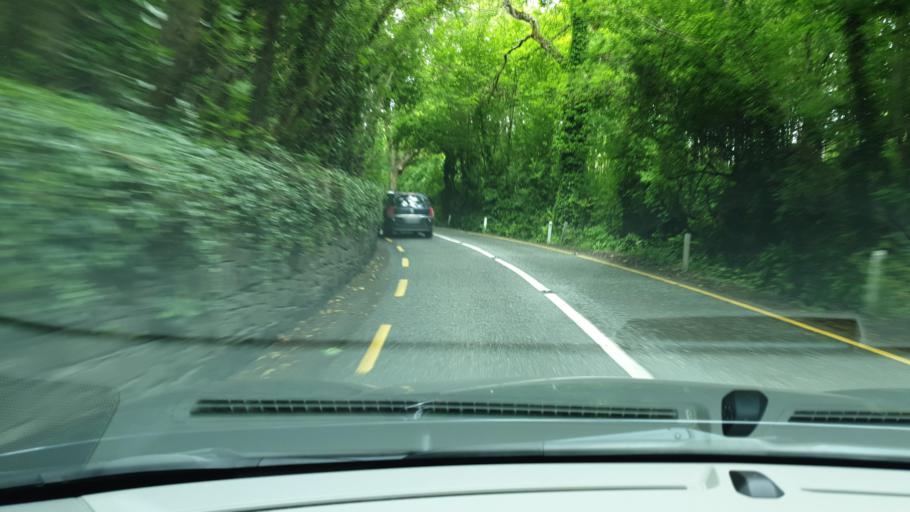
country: IE
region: Leinster
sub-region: Kildare
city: Leixlip
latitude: 53.3815
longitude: -6.5295
